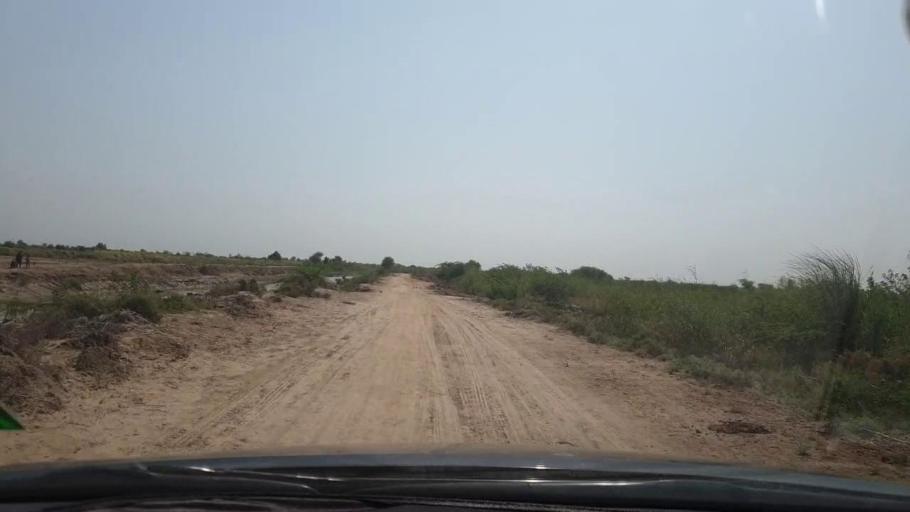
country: PK
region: Sindh
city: Tando Bago
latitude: 24.7905
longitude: 69.1155
